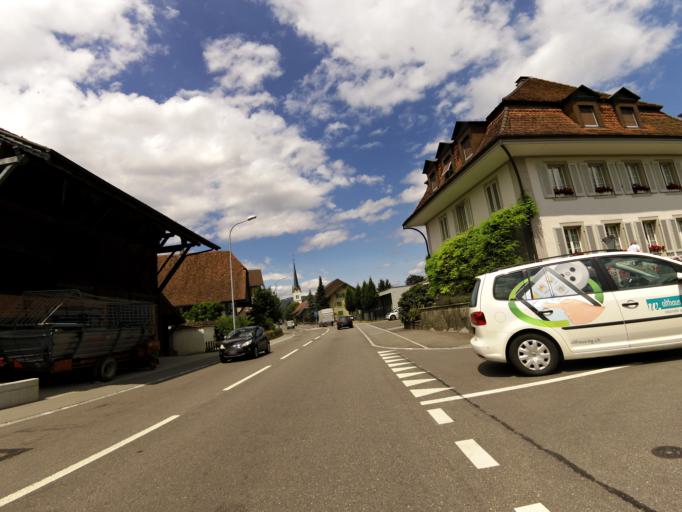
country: CH
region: Bern
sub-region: Oberaargau
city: Aarwangen
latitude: 47.2408
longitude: 7.7682
